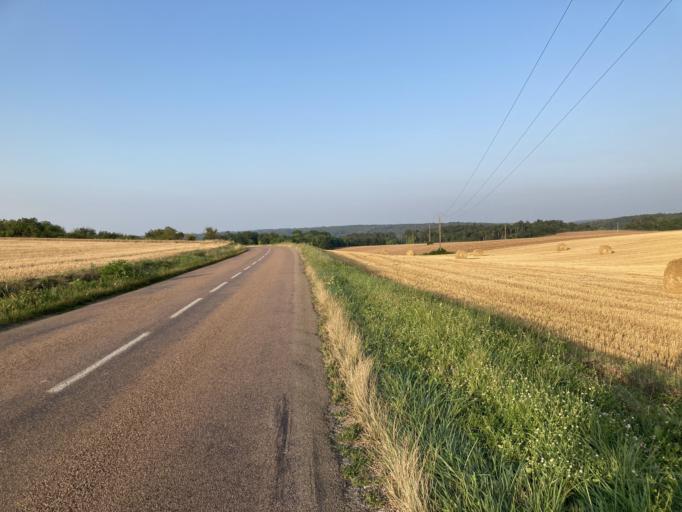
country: FR
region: Bourgogne
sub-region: Departement de l'Yonne
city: Vermenton
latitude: 47.5983
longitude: 3.6506
